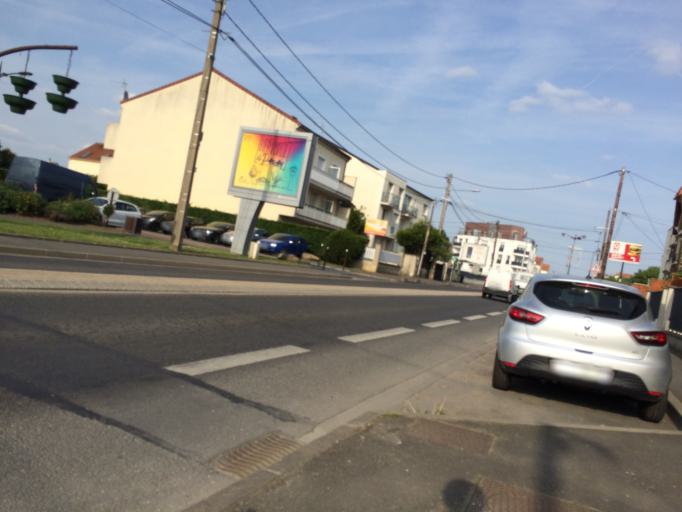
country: FR
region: Ile-de-France
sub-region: Departement de l'Essonne
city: Paray-Vieille-Poste
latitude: 48.7055
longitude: 2.3535
